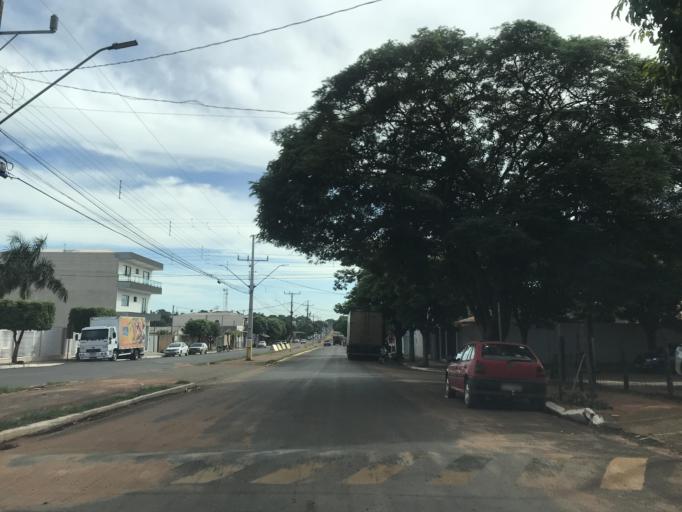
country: BR
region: Parana
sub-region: Paranavai
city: Nova Aurora
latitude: -22.9412
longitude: -52.6905
